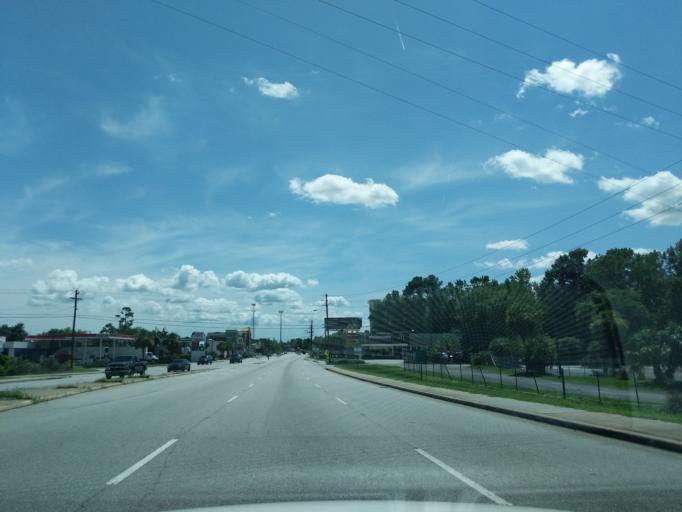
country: US
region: South Carolina
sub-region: Charleston County
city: North Charleston
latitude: 32.8702
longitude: -80.0123
